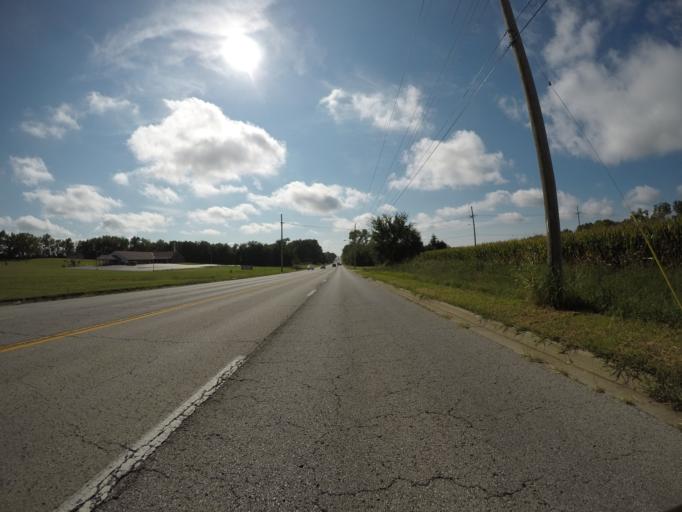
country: US
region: Kansas
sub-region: Leavenworth County
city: Basehor
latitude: 39.1287
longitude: -94.8818
